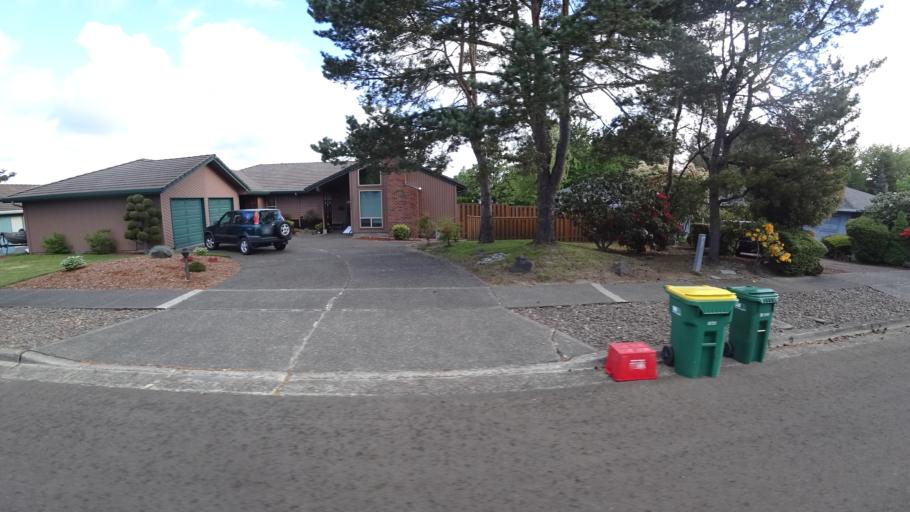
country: US
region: Oregon
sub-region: Washington County
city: Beaverton
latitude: 45.4743
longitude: -122.8234
